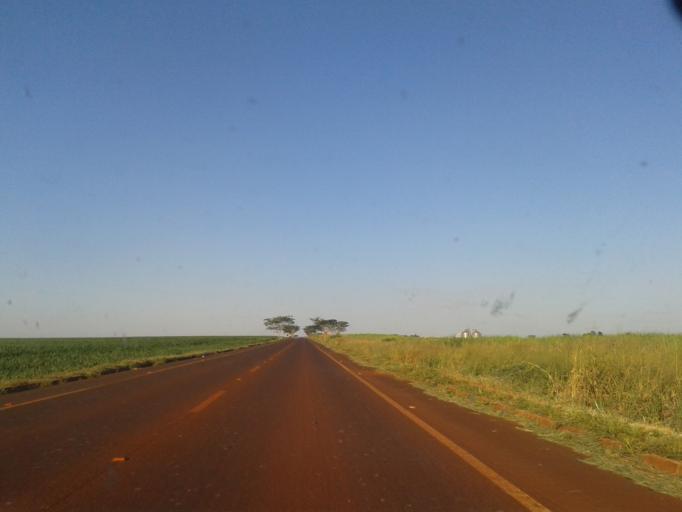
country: BR
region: Minas Gerais
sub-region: Capinopolis
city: Capinopolis
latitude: -18.7002
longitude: -49.6536
